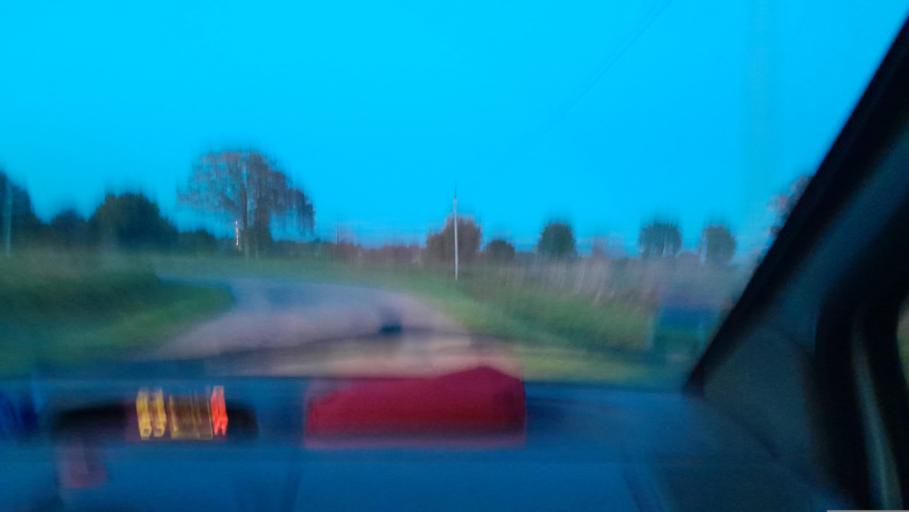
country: FR
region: Brittany
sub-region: Departement d'Ille-et-Vilaine
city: Rannee
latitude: 47.8763
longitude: -1.1836
